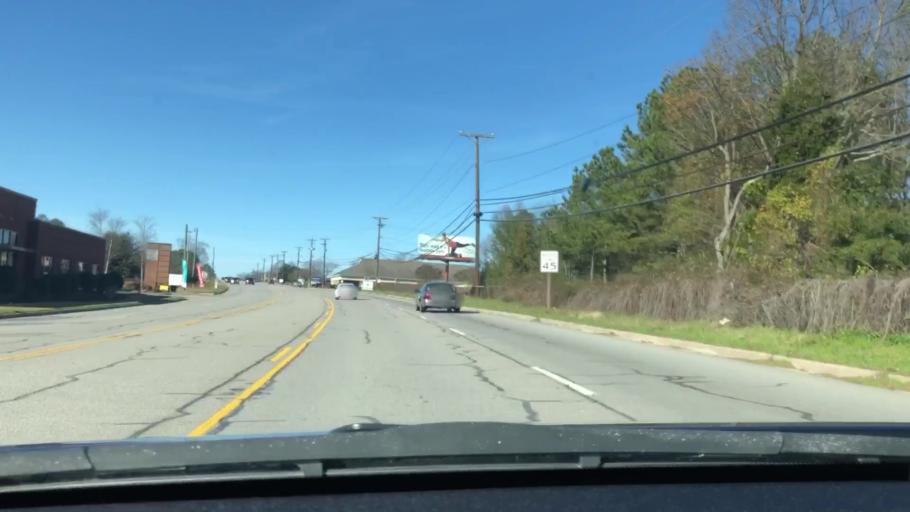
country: US
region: South Carolina
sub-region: Lexington County
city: Oak Grove
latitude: 34.0079
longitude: -81.1271
